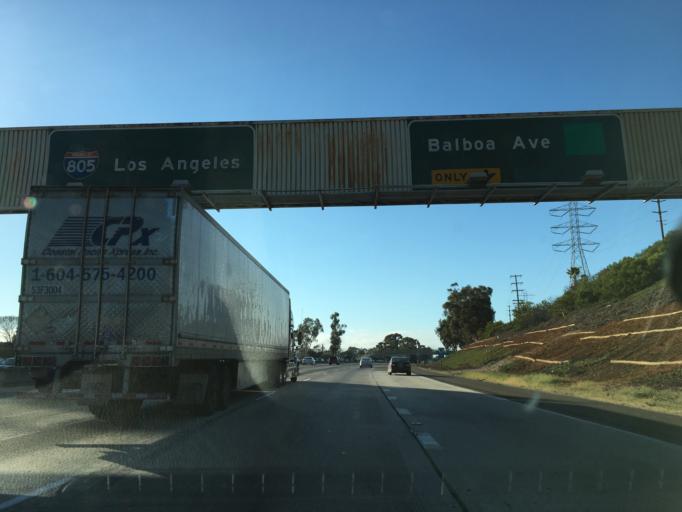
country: US
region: California
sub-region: San Diego County
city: San Diego
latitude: 32.8136
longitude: -117.1570
